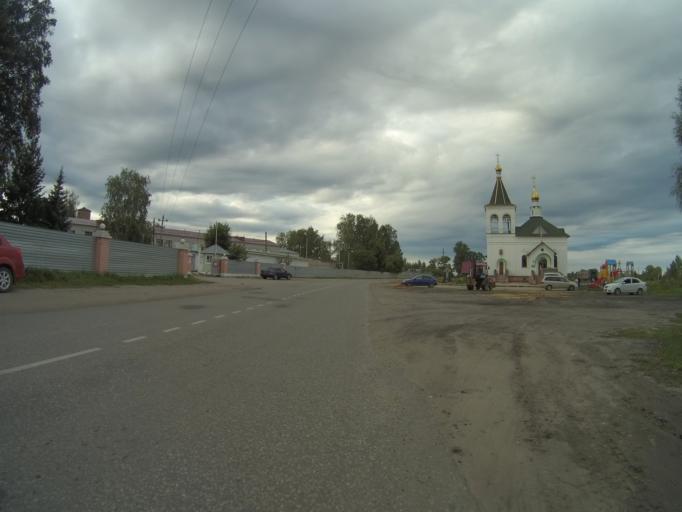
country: RU
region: Vladimir
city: Golovino
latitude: 55.9479
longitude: 40.4430
